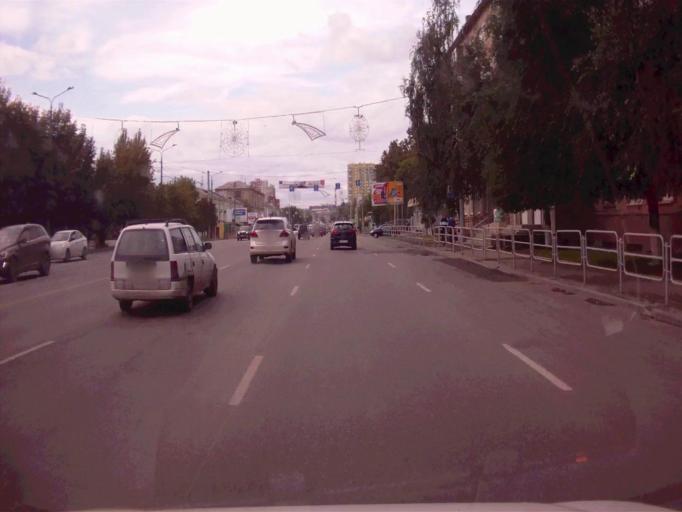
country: RU
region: Chelyabinsk
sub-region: Gorod Chelyabinsk
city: Chelyabinsk
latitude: 55.1406
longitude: 61.3956
